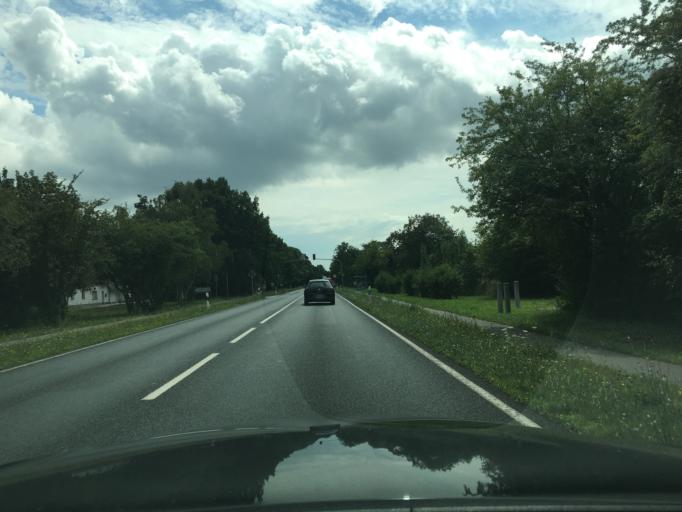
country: DE
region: Saxony-Anhalt
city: Wolfen
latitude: 51.6452
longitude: 12.2769
